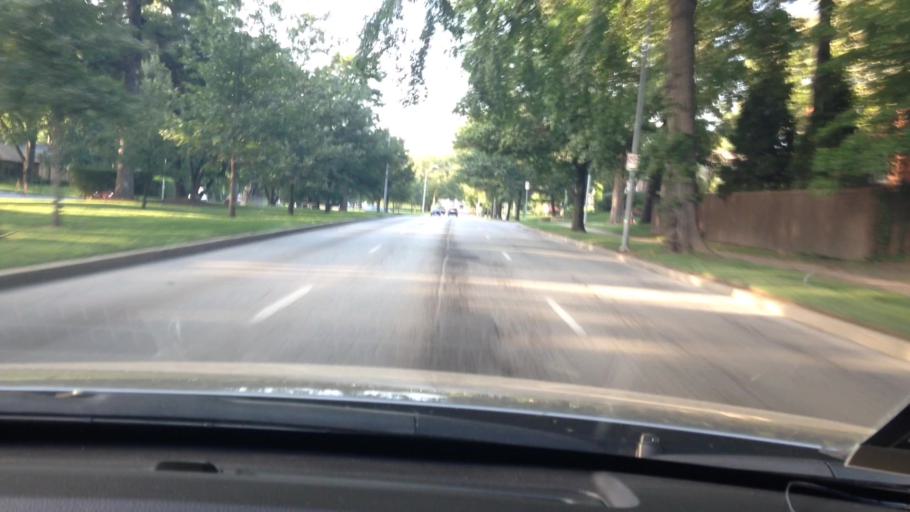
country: US
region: Kansas
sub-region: Johnson County
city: Mission Hills
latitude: 39.0069
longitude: -94.6026
